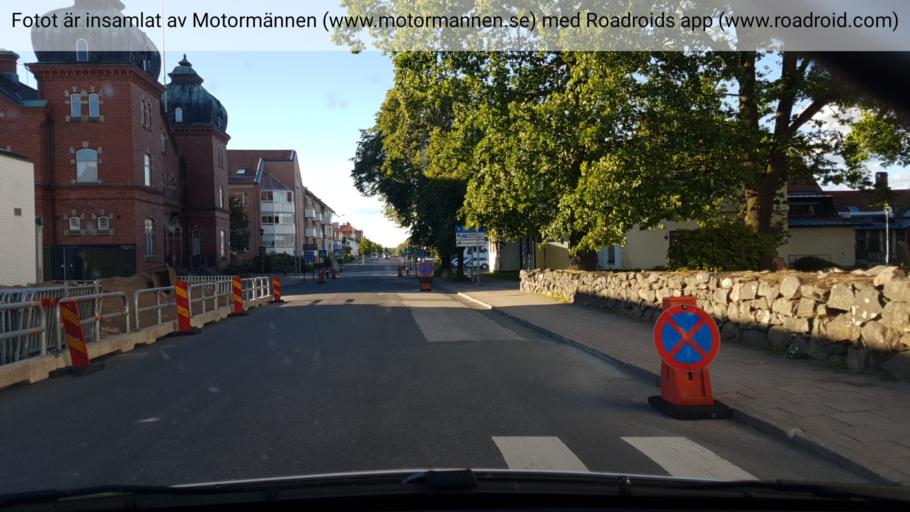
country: SE
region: Vaestra Goetaland
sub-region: Tidaholms Kommun
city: Tidaholm
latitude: 58.1809
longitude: 13.9594
